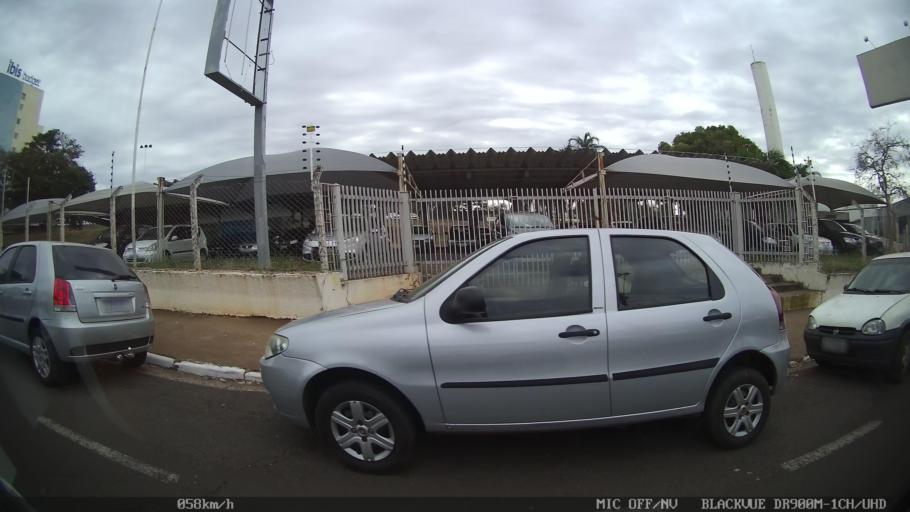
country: BR
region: Sao Paulo
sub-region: Sao Jose Do Rio Preto
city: Sao Jose do Rio Preto
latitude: -20.8246
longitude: -49.4045
